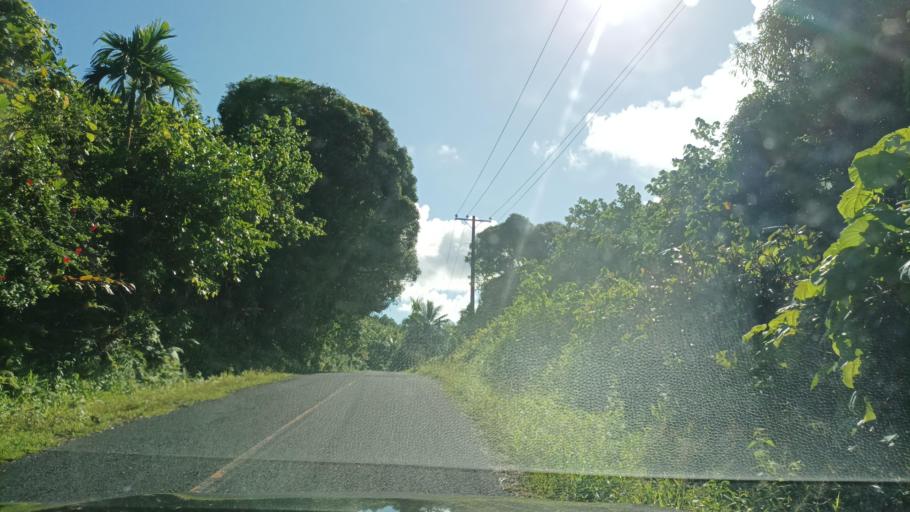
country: FM
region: Pohnpei
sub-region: Madolenihm Municipality
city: Madolenihm Municipality Government
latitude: 6.8081
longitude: 158.2808
